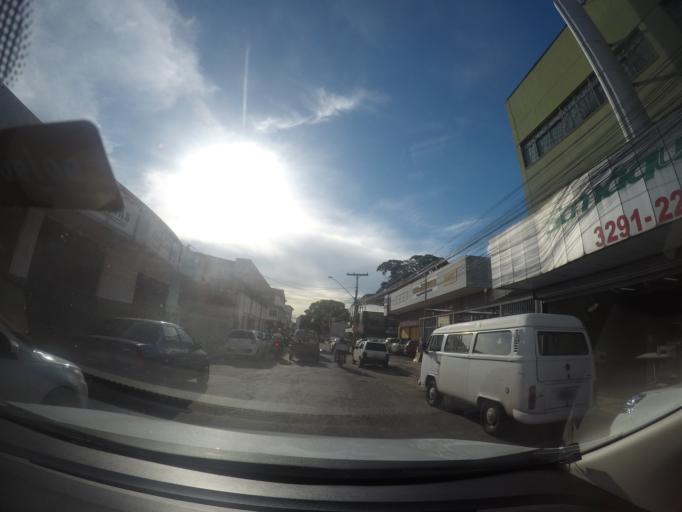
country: BR
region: Goias
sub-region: Goiania
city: Goiania
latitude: -16.6740
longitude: -49.2866
